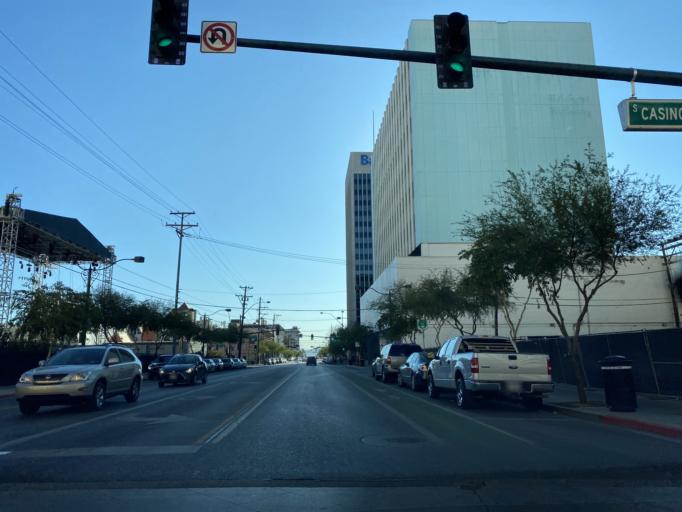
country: US
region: Nevada
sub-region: Clark County
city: Las Vegas
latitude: 36.1684
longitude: -115.1455
